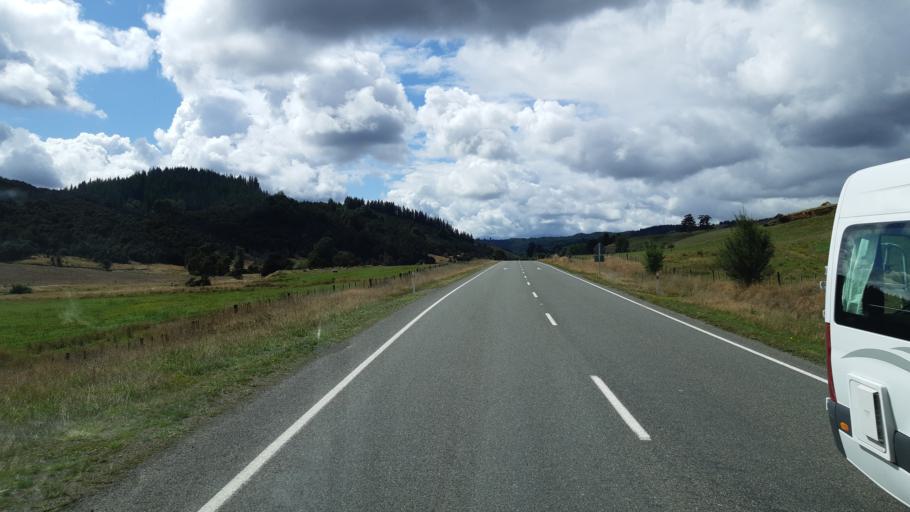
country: NZ
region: Tasman
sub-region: Tasman District
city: Wakefield
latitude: -41.6422
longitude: 172.6617
